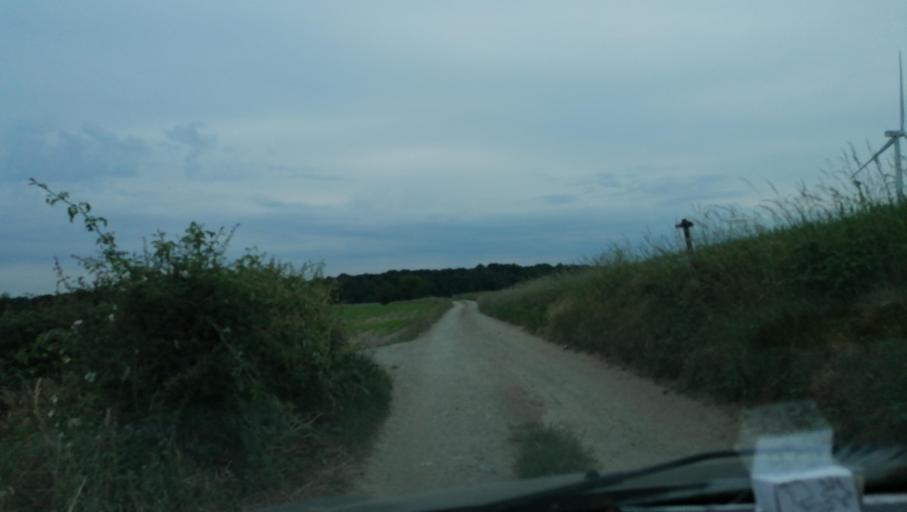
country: BE
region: Wallonia
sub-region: Province du Hainaut
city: Beaumont
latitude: 50.2083
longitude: 4.1623
